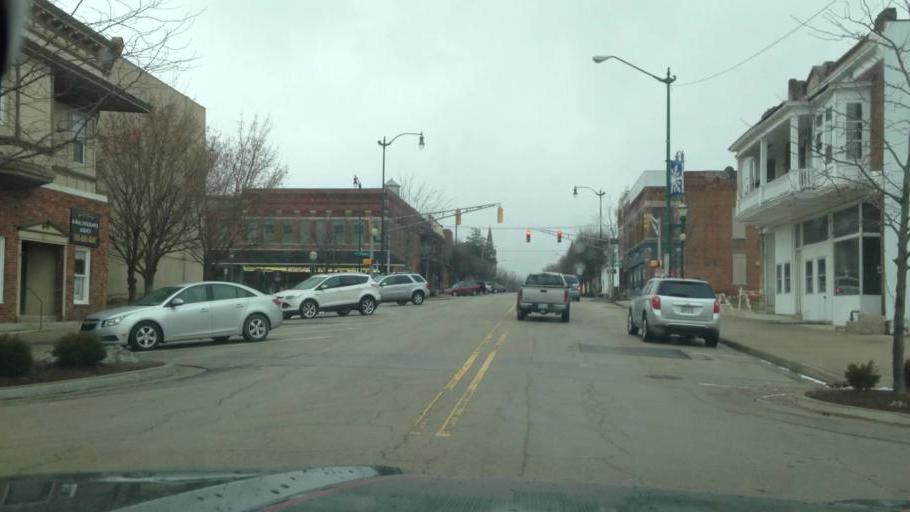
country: US
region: Ohio
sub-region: Darke County
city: Union City
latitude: 40.2003
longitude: -84.8069
